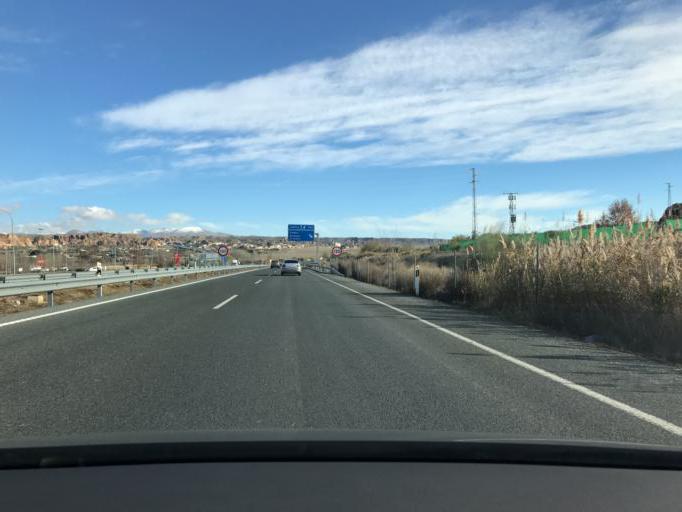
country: ES
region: Andalusia
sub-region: Provincia de Granada
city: Guadix
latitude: 37.3201
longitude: -3.1546
